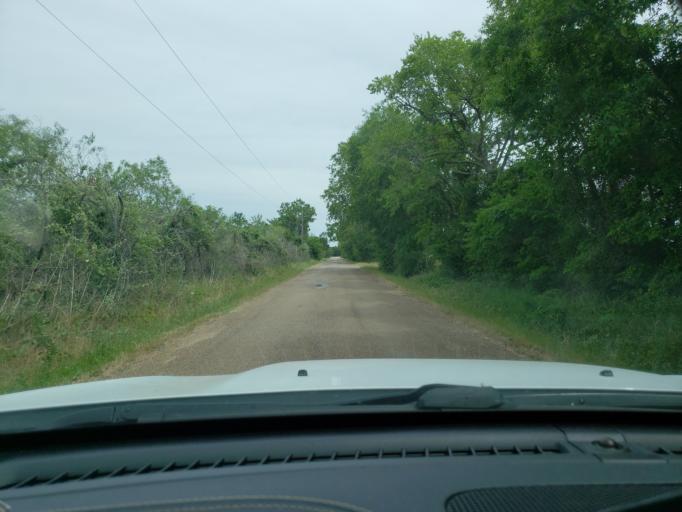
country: US
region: Texas
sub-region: Burleson County
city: Somerville
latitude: 30.3520
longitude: -96.5441
